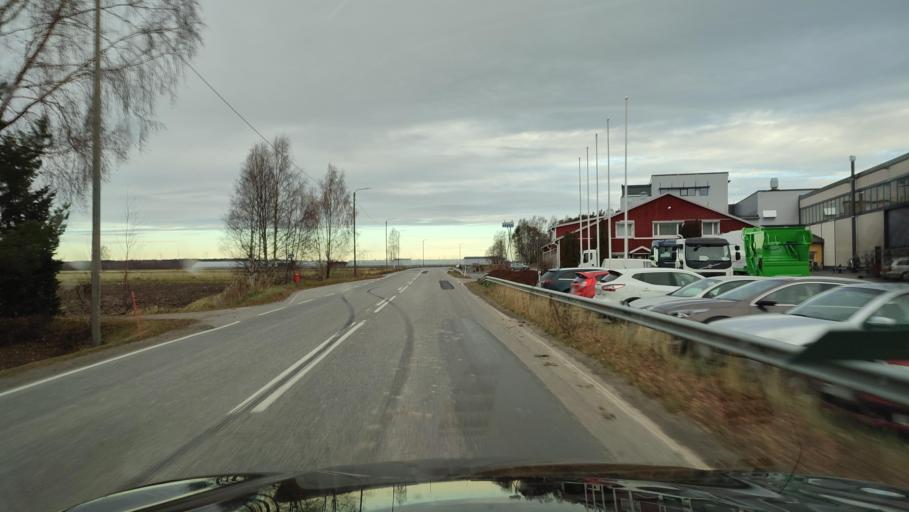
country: FI
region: Ostrobothnia
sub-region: Sydosterbotten
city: Naerpes
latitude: 62.4416
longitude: 21.3511
